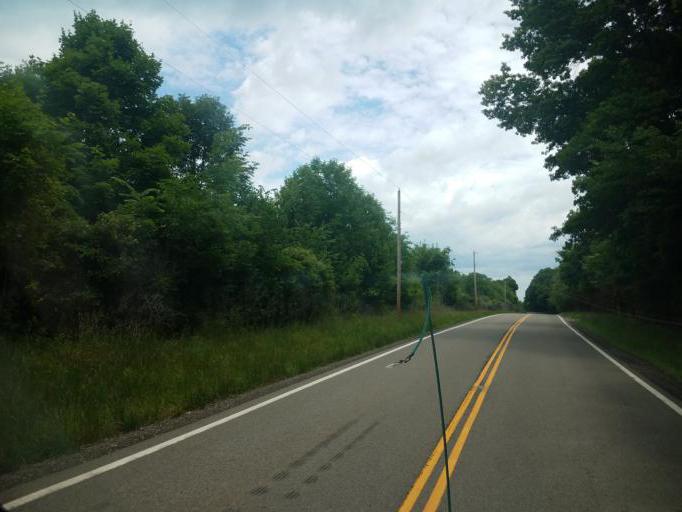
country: US
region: Ohio
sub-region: Huron County
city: Plymouth
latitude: 40.9472
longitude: -82.7047
